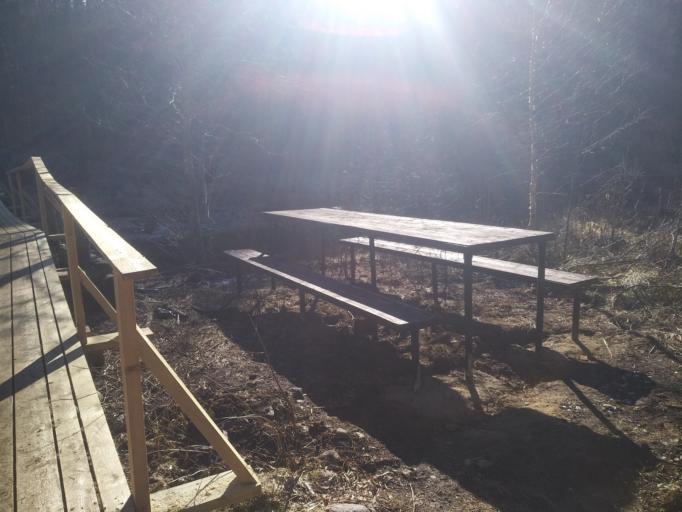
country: RU
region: Leningrad
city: Sapernoye
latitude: 60.6279
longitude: 30.0707
